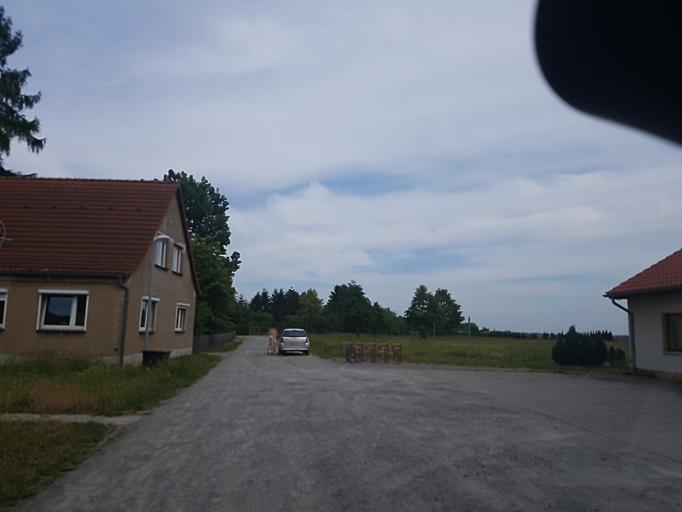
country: DE
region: Brandenburg
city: Gorzke
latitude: 52.1083
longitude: 12.3685
